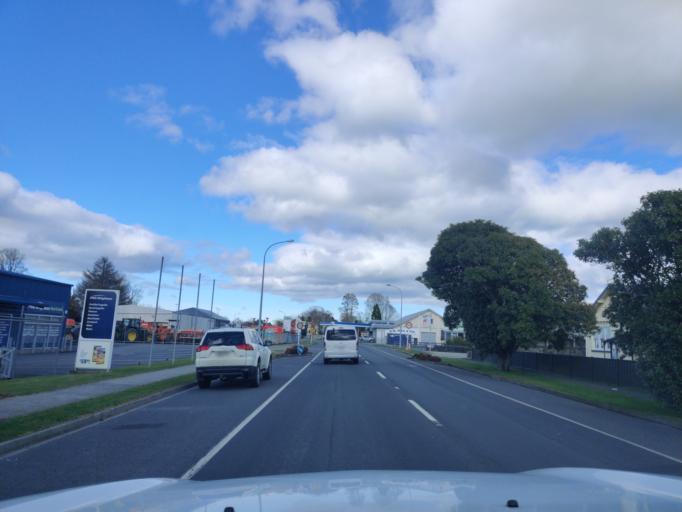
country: NZ
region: Waikato
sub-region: Matamata-Piako District
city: Matamata
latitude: -37.8127
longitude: 175.7706
